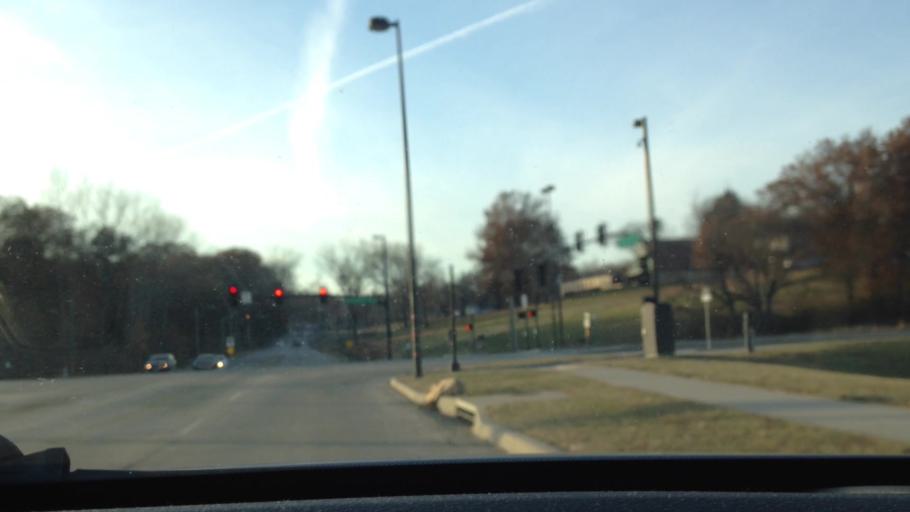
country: US
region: Missouri
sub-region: Clay County
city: North Kansas City
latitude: 39.1623
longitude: -94.5318
